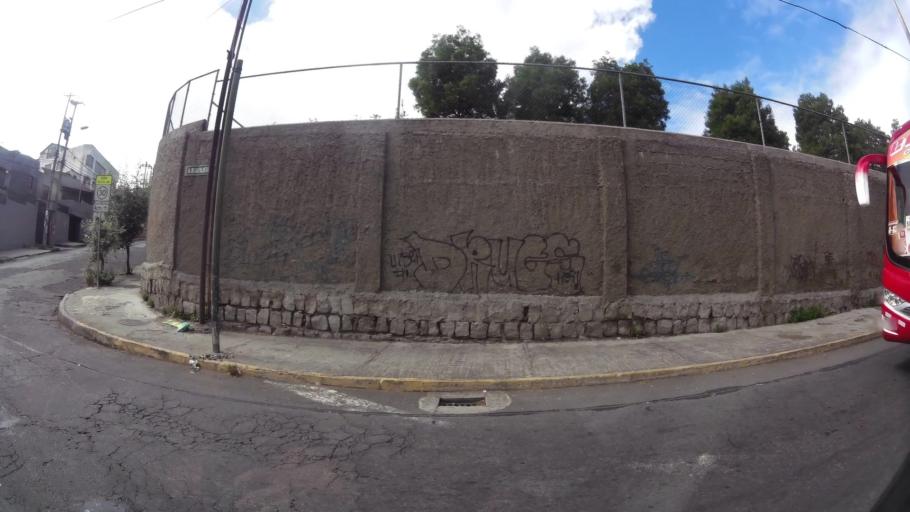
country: EC
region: Pichincha
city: Quito
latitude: -0.1576
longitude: -78.4723
